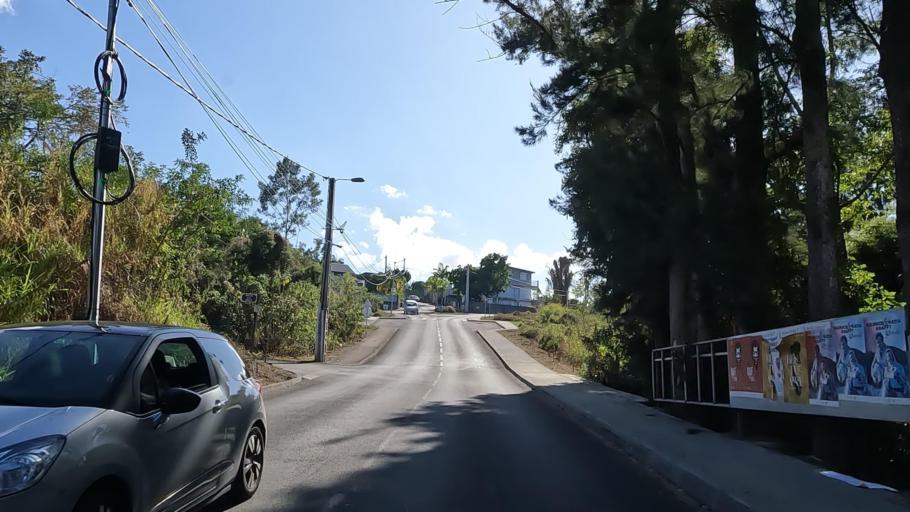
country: RE
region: Reunion
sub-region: Reunion
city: Le Tampon
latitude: -21.2589
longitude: 55.5118
